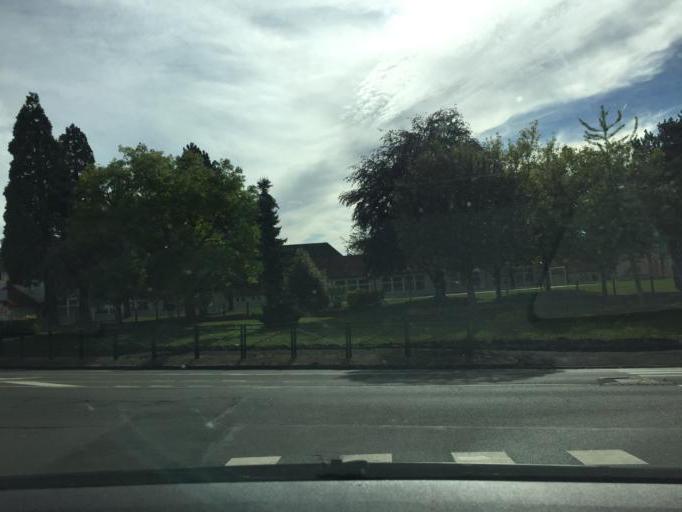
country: FR
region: Ile-de-France
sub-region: Departement de l'Essonne
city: Orsay
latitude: 48.6864
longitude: 2.1873
